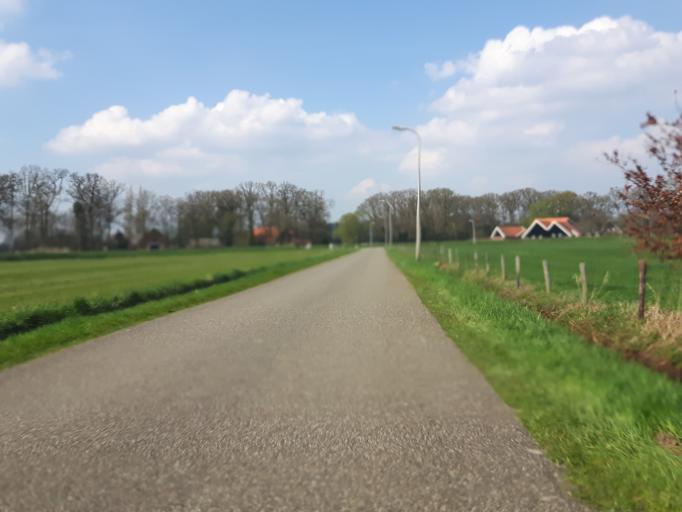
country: NL
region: Overijssel
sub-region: Gemeente Hengelo
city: Hengelo
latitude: 52.1971
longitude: 6.7947
